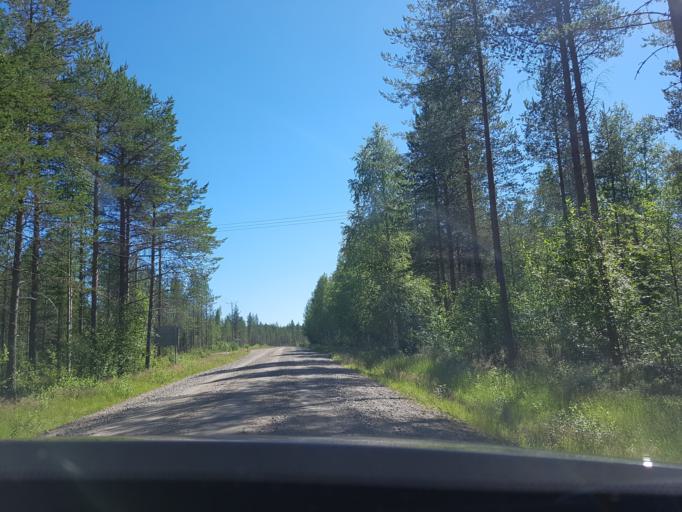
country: FI
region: Kainuu
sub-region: Kehys-Kainuu
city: Kuhmo
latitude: 64.1825
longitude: 29.5920
